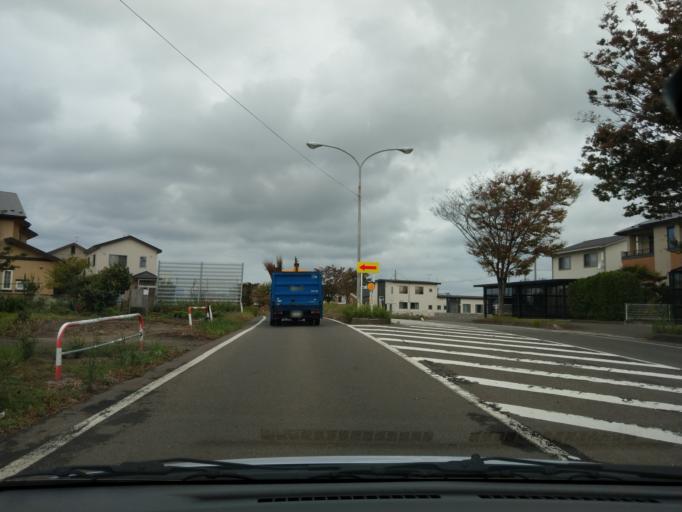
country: JP
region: Akita
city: Akita Shi
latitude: 39.6785
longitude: 140.0775
